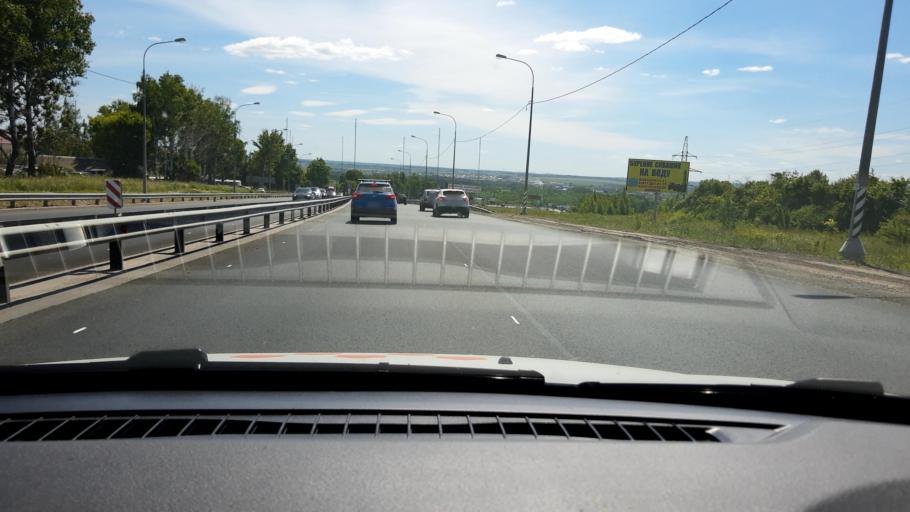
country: RU
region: Nizjnij Novgorod
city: Burevestnik
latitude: 56.1932
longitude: 43.9230
